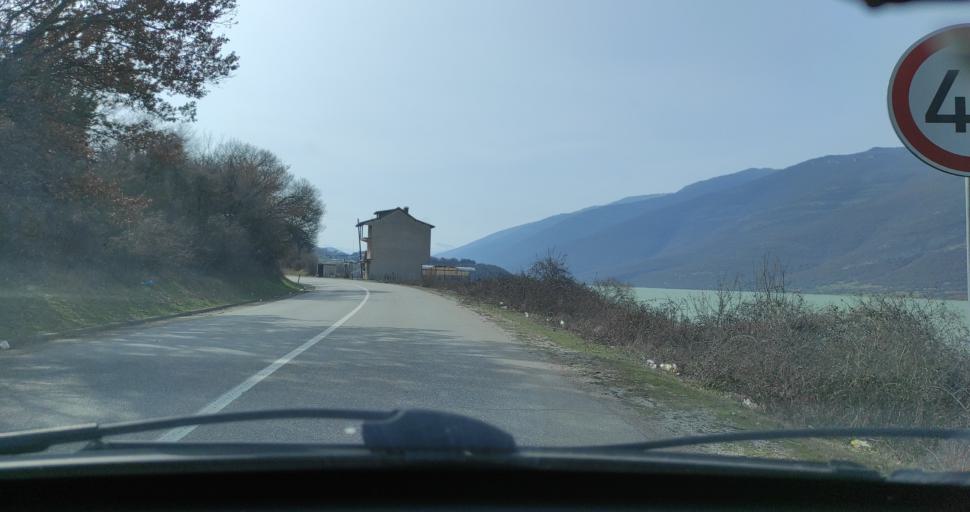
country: AL
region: Kukes
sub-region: Rrethi i Kukesit
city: Zapod
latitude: 42.1620
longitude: 20.5594
